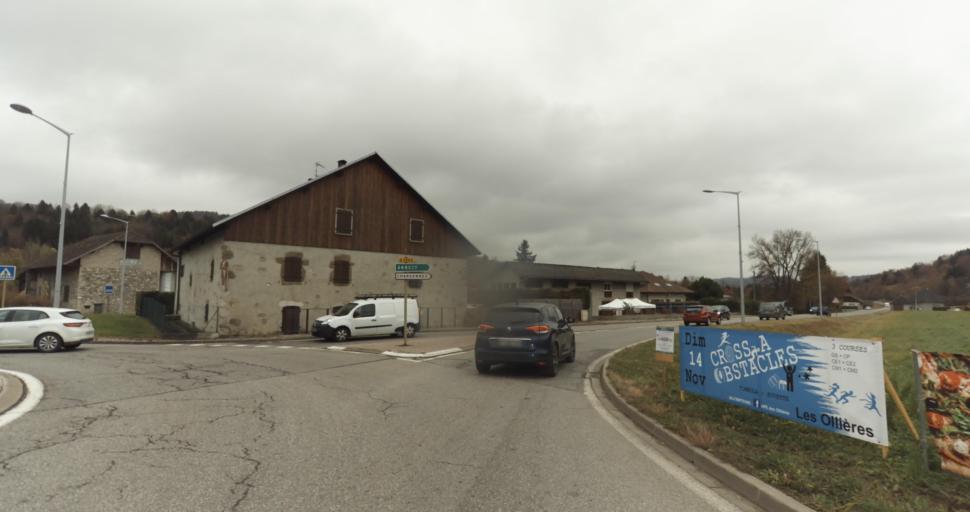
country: FR
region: Rhone-Alpes
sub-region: Departement de la Haute-Savoie
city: Groisy
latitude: 45.9999
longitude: 6.1800
